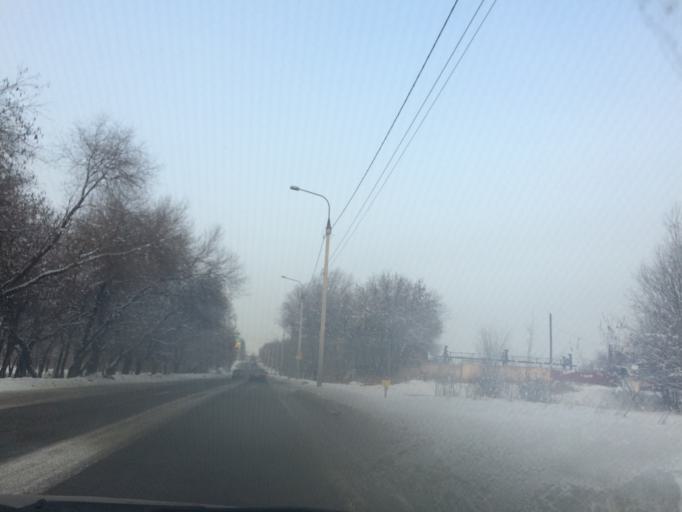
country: RU
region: Chelyabinsk
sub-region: Gorod Magnitogorsk
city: Magnitogorsk
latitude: 53.4670
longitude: 59.0734
